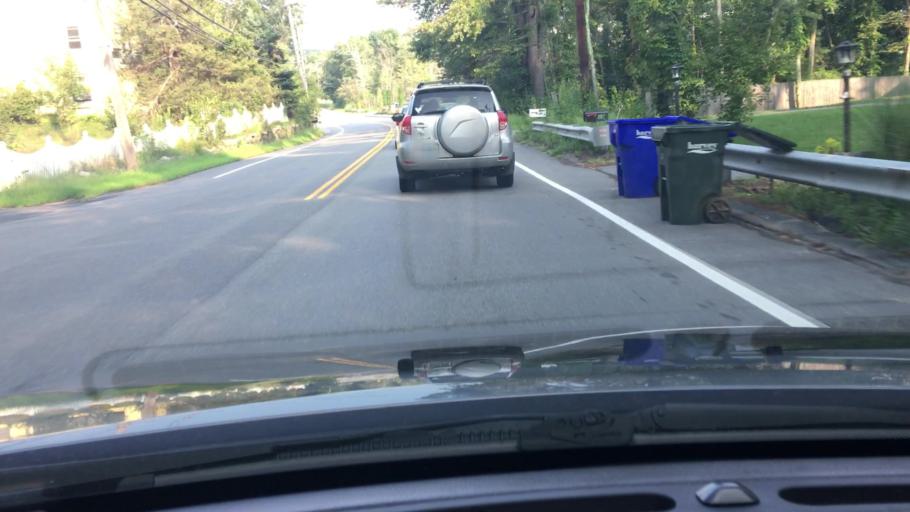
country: US
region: Massachusetts
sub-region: Middlesex County
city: Hopkinton
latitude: 42.2285
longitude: -71.5439
